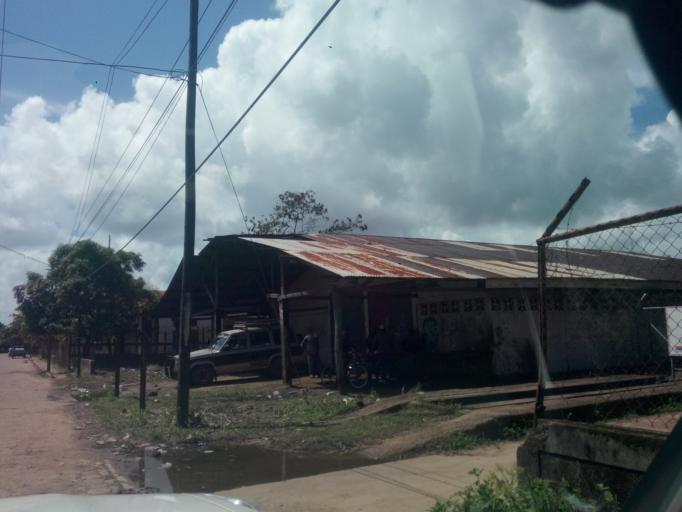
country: NI
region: Atlantico Norte (RAAN)
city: Puerto Cabezas
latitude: 14.0361
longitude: -83.3939
